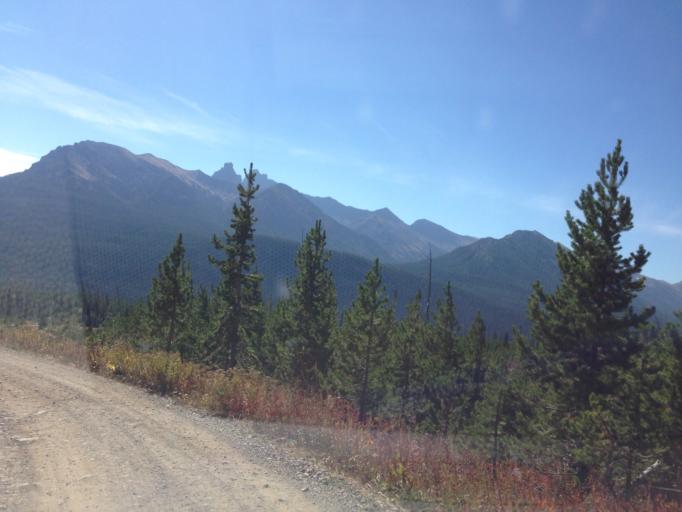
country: US
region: Montana
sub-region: Stillwater County
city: Absarokee
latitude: 45.0374
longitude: -109.9142
